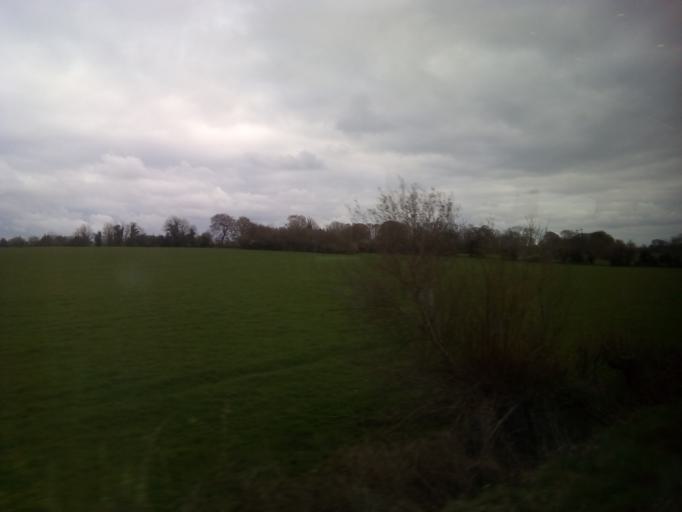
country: IE
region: Leinster
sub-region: An Longfort
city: Longford
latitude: 53.7767
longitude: -7.8335
